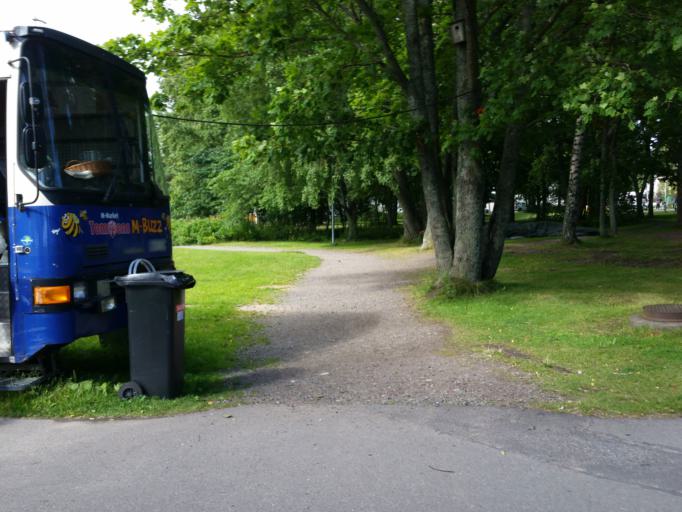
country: FI
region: Uusimaa
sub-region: Raaseporin
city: Hanko
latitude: 59.8208
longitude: 22.9671
